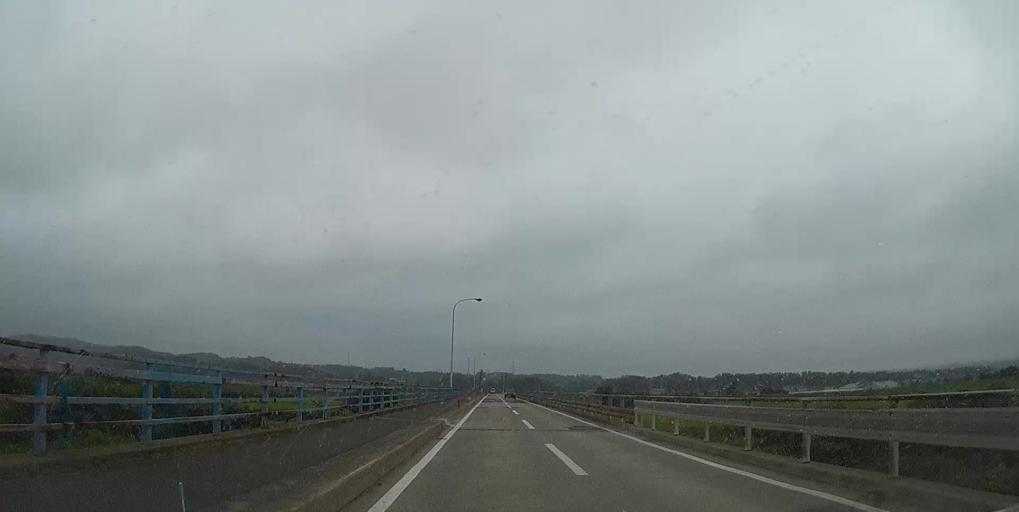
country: JP
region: Hokkaido
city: Iwanai
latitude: 42.4216
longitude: 140.0206
